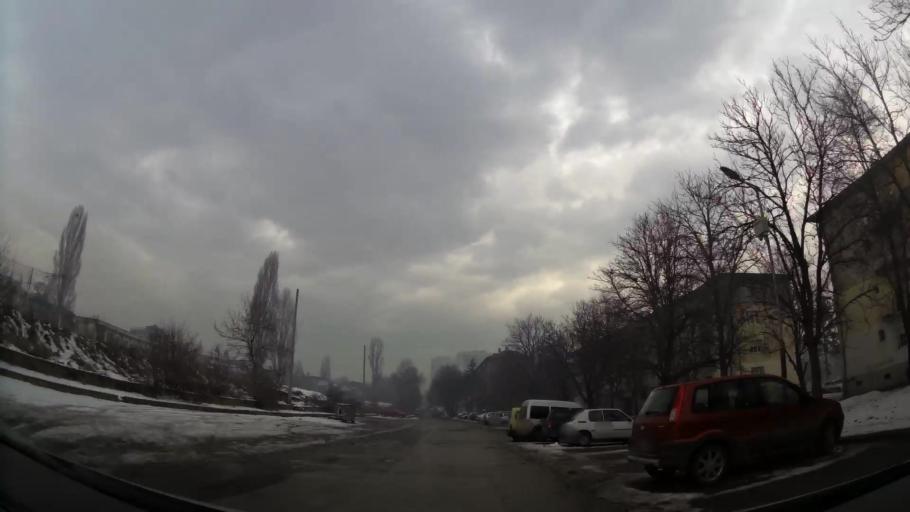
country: BG
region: Sofia-Capital
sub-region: Stolichna Obshtina
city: Sofia
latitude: 42.6938
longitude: 23.2771
